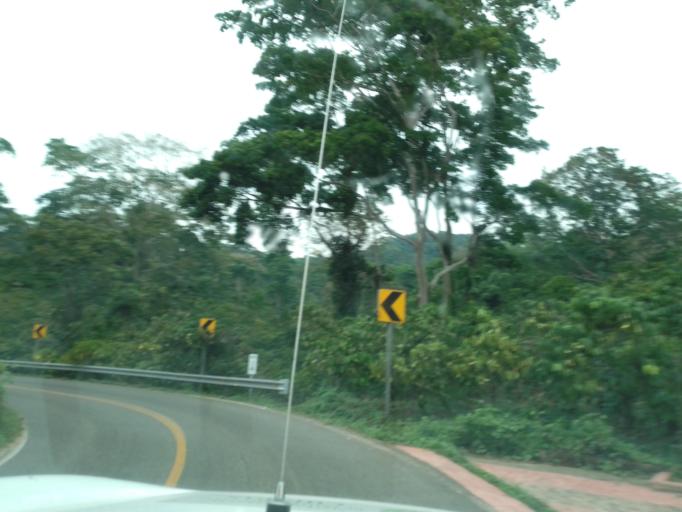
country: MX
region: Chiapas
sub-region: Union Juarez
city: Santo Domingo
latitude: 15.0381
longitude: -92.1244
